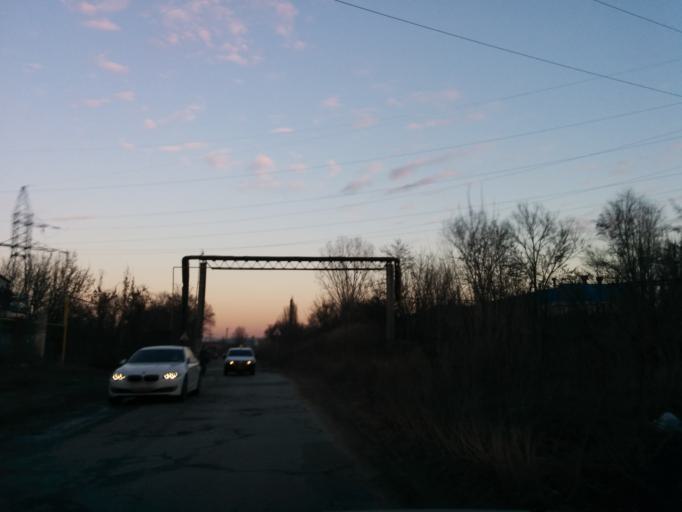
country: MD
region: Chisinau
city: Chisinau
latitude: 47.0444
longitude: 28.8053
